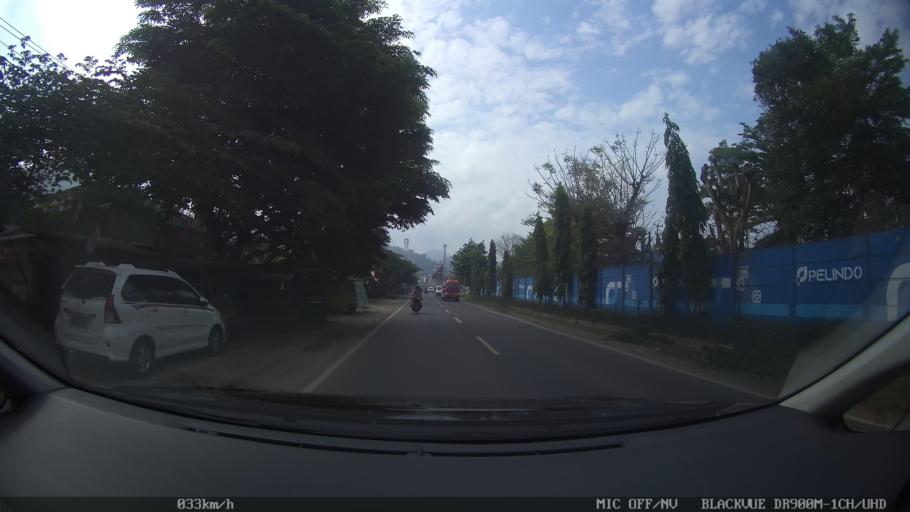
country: ID
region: Lampung
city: Panjang
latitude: -5.4674
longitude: 105.3203
